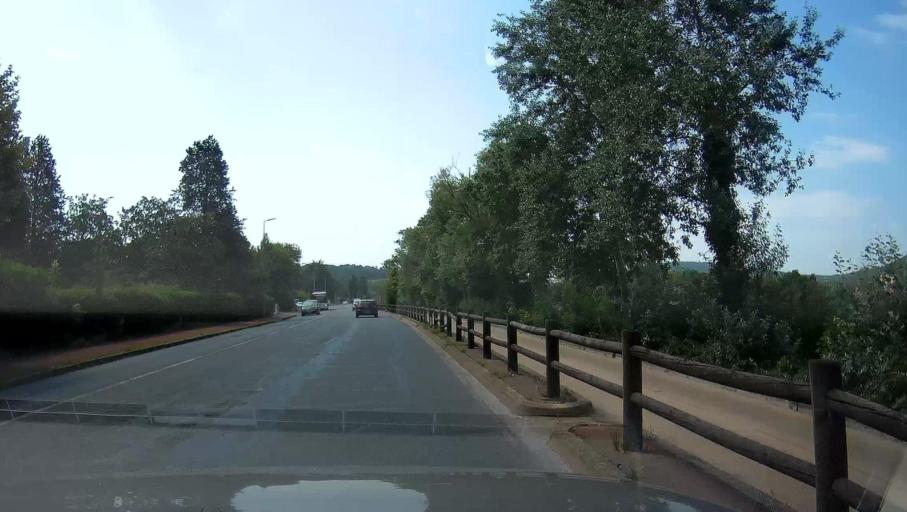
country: FR
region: Rhone-Alpes
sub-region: Departement du Rhone
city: Fleurieu-sur-Saone
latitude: 45.8656
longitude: 4.8397
